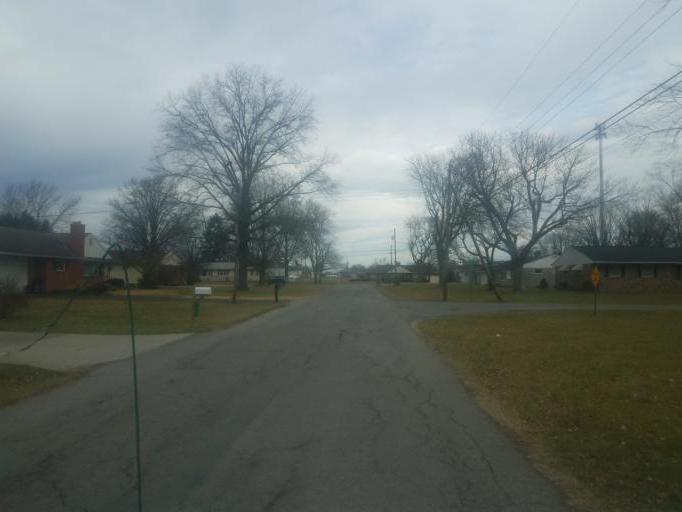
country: US
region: Ohio
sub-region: Marion County
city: Marion
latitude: 40.5783
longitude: -83.0971
